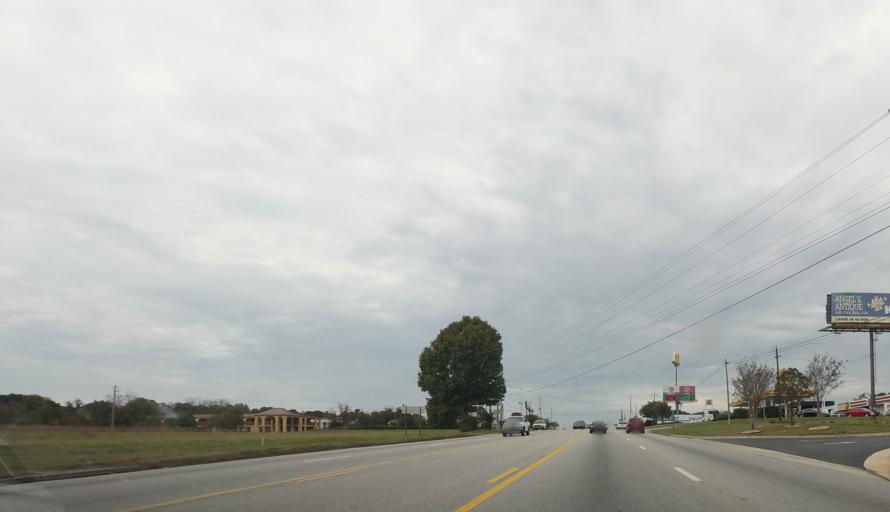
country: US
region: Alabama
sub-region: Lee County
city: Opelika
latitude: 32.6434
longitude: -85.3478
